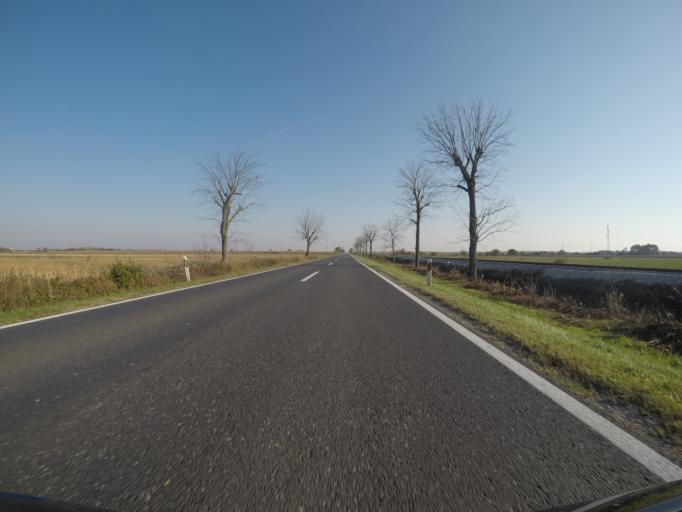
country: HR
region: Koprivnicko-Krizevacka
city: Kalinovac
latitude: 46.0189
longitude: 17.0867
